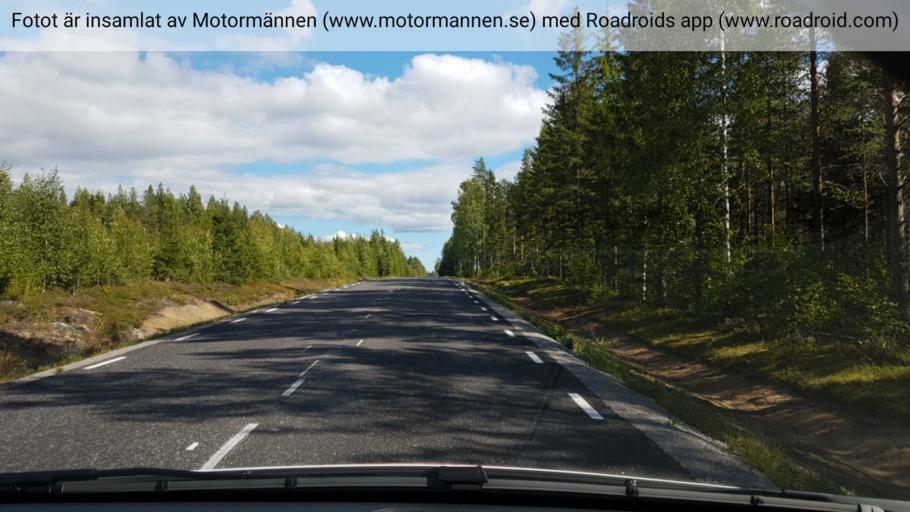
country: SE
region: Vaesterbotten
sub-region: Umea Kommun
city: Hoernefors
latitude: 63.6992
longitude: 19.7351
